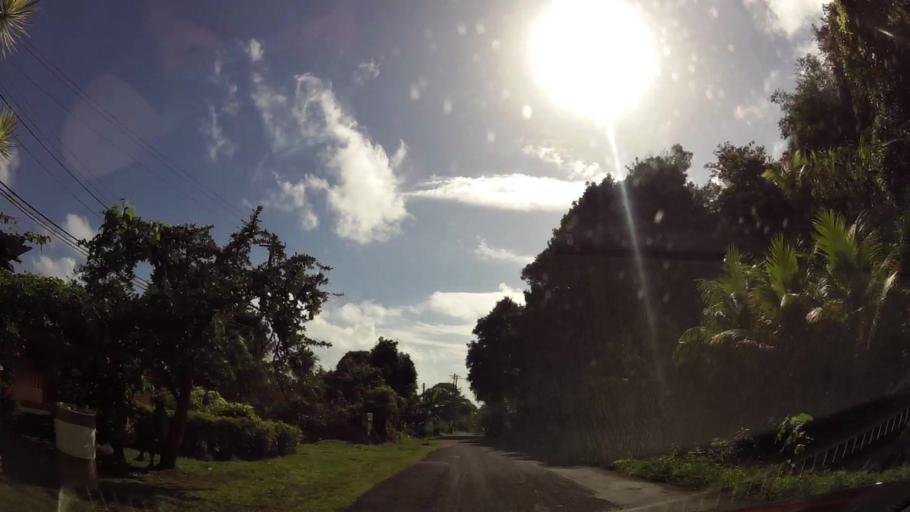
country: DM
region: Saint David
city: Castle Bruce
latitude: 15.4801
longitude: -61.2524
